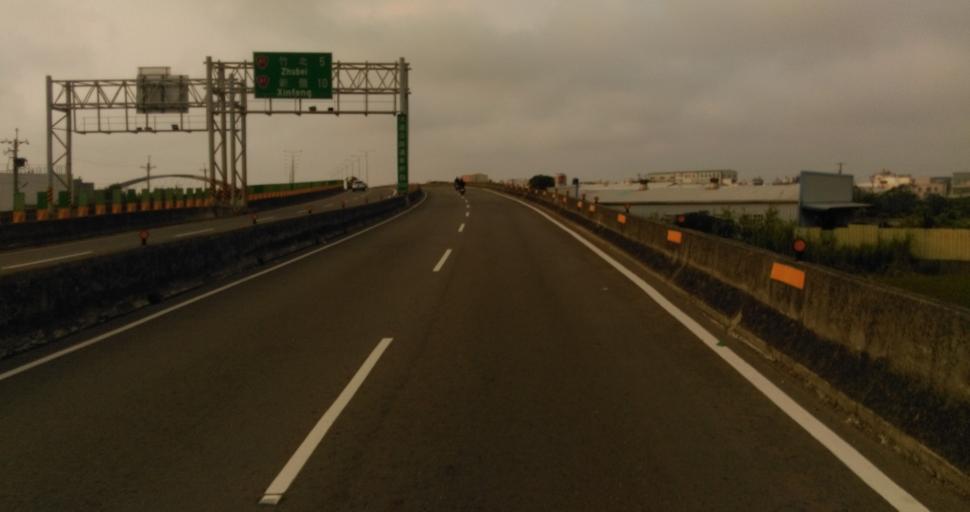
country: TW
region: Taiwan
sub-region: Hsinchu
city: Hsinchu
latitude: 24.8023
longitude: 120.9206
